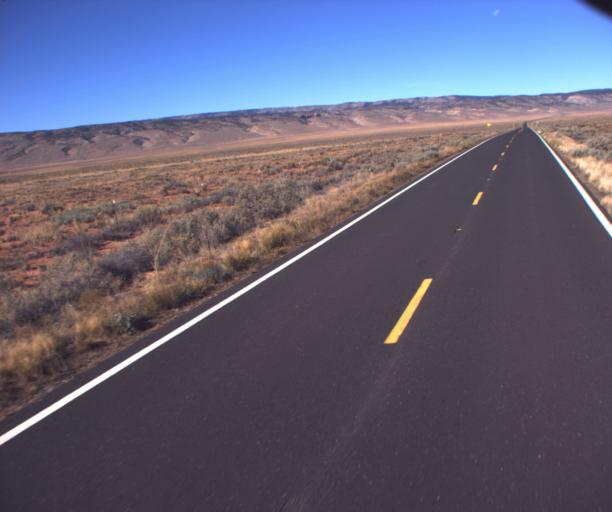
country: US
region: Arizona
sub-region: Coconino County
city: Page
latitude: 36.7129
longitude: -111.9812
